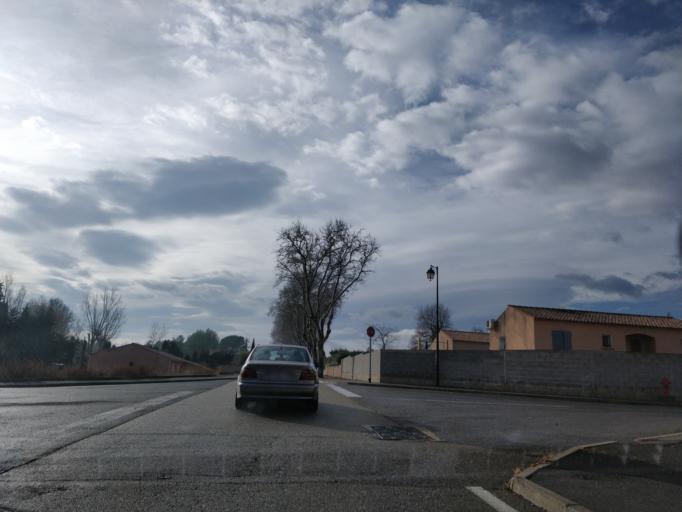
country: FR
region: Languedoc-Roussillon
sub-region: Departement du Gard
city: Villevieille
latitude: 43.8175
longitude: 4.1244
